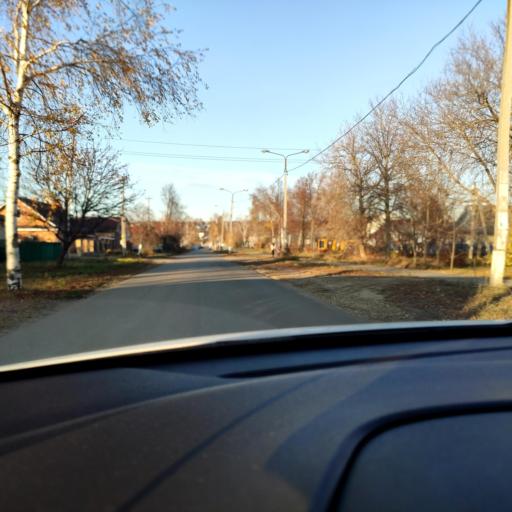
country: RU
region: Tatarstan
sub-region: Gorod Kazan'
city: Kazan
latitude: 55.8793
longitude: 49.0699
